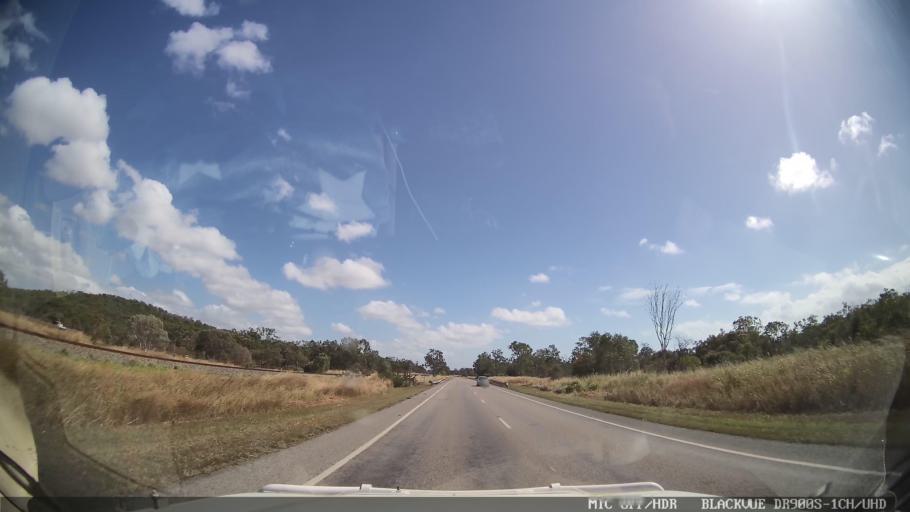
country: AU
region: Queensland
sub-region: Whitsunday
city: Bowen
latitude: -20.1811
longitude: 148.3511
